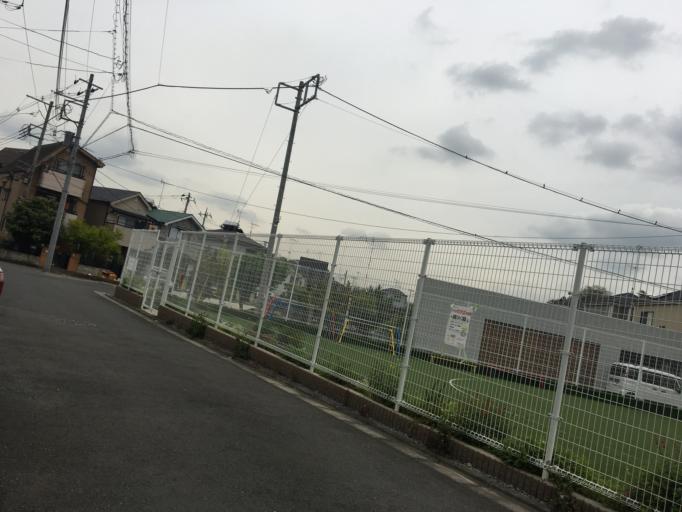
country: JP
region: Saitama
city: Oi
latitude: 35.8505
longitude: 139.5445
